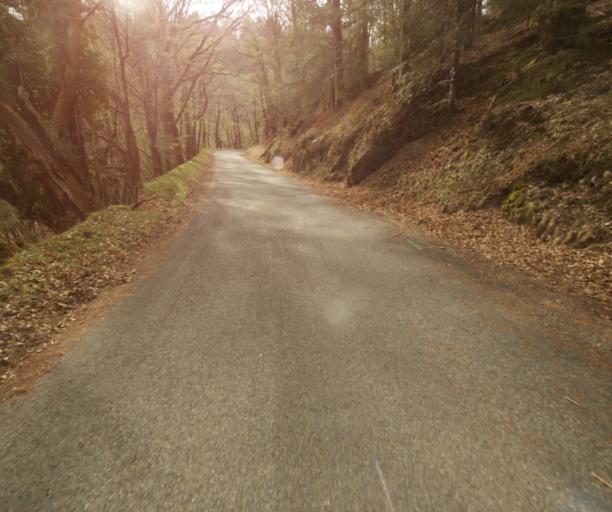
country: FR
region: Limousin
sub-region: Departement de la Correze
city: Argentat
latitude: 45.1970
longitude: 1.9785
